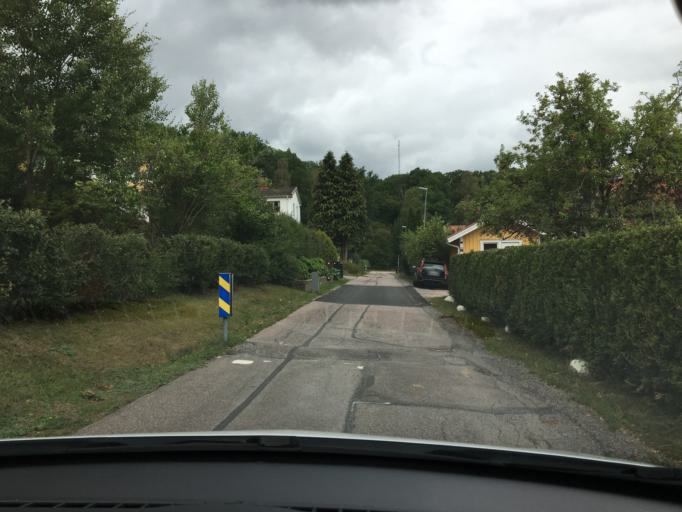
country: SE
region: Vaestra Goetaland
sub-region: Ale Kommun
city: Alafors
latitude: 57.9234
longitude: 12.0956
